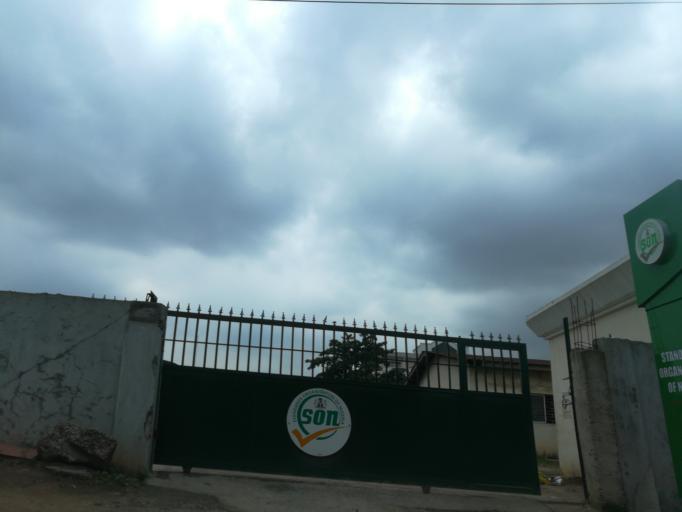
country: NG
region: Lagos
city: Agege
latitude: 6.6231
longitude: 3.3451
